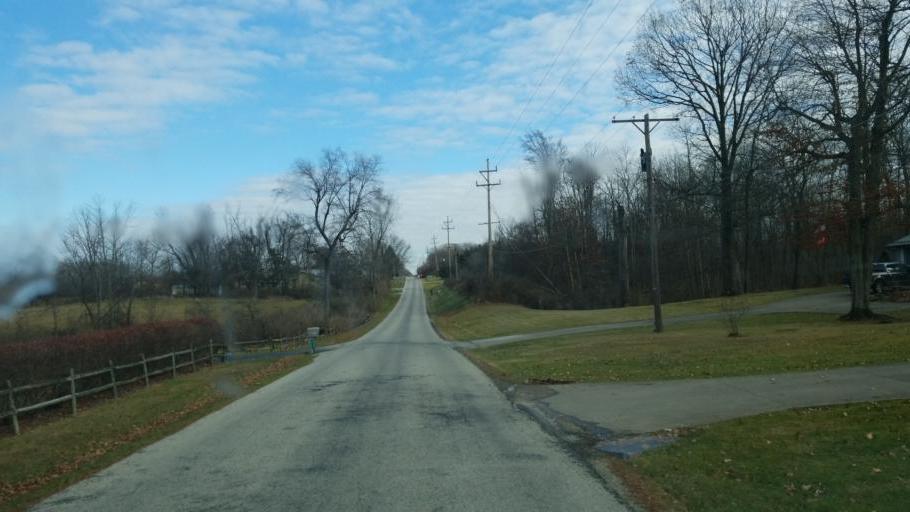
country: US
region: Ohio
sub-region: Richland County
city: Ontario
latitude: 40.7838
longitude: -82.6580
